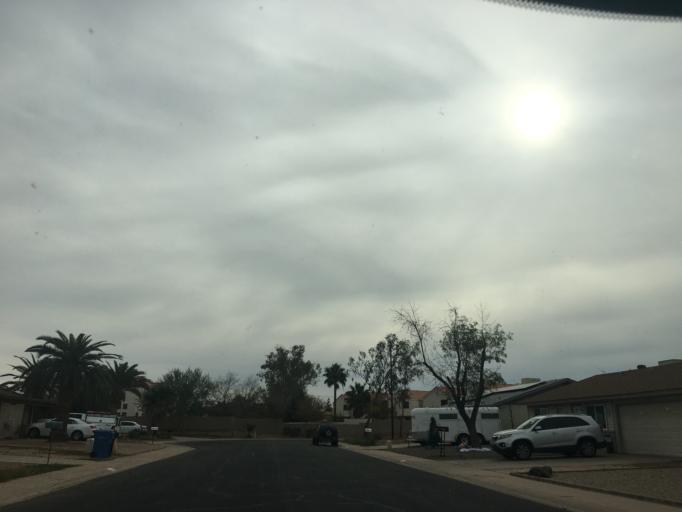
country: US
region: Arizona
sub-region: Maricopa County
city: Gilbert
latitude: 33.3635
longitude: -111.7945
